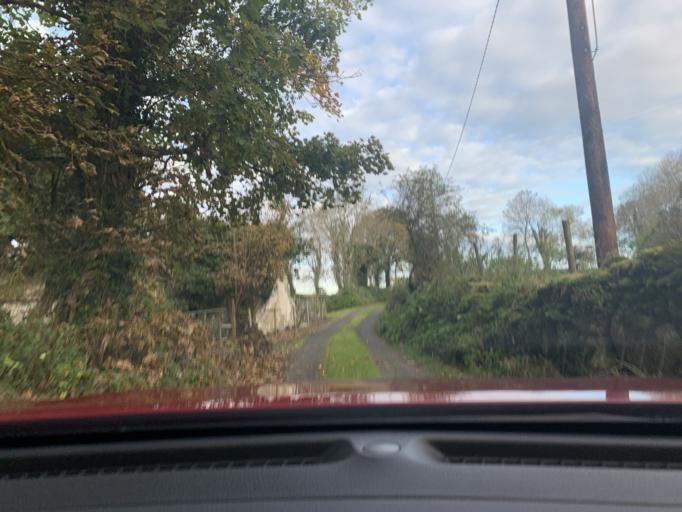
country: IE
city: Ballisodare
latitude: 54.2324
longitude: -8.5030
